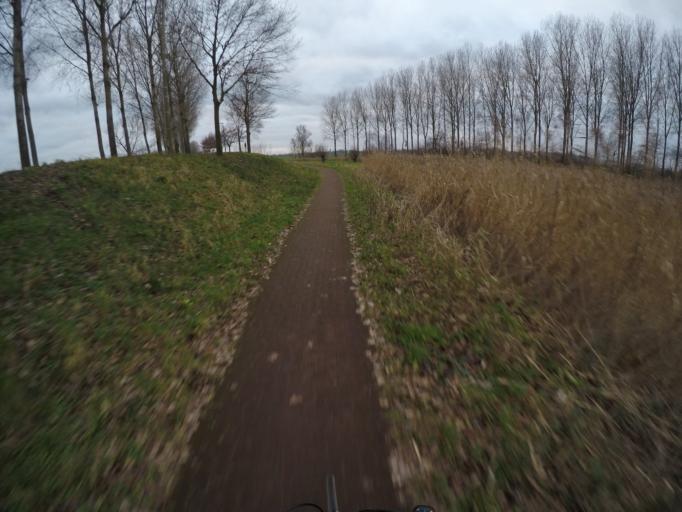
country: BE
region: Flanders
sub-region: Provincie Oost-Vlaanderen
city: Sint-Gillis-Waas
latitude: 51.2401
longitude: 4.1468
